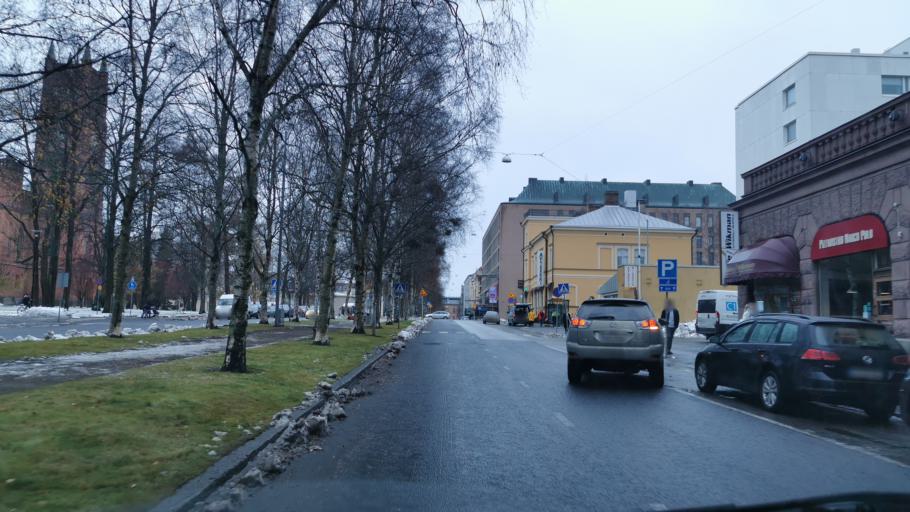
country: FI
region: Ostrobothnia
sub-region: Vaasa
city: Vaasa
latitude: 63.0958
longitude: 21.6117
